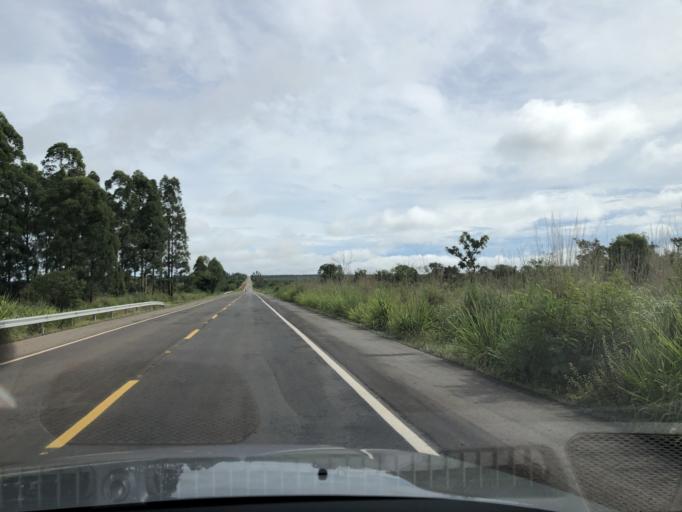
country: BR
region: Federal District
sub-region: Brasilia
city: Brasilia
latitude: -15.6715
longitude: -48.0880
